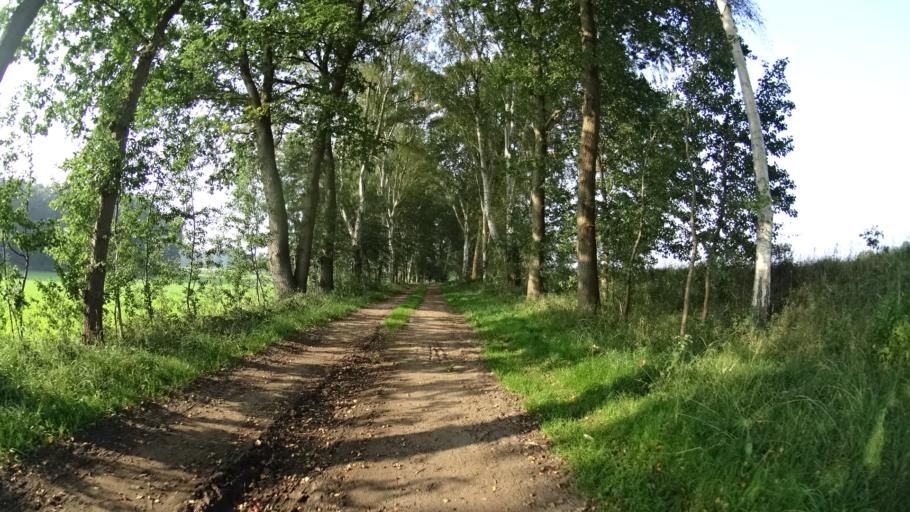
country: DE
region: Lower Saxony
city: Reppenstedt
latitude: 53.2327
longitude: 10.3639
